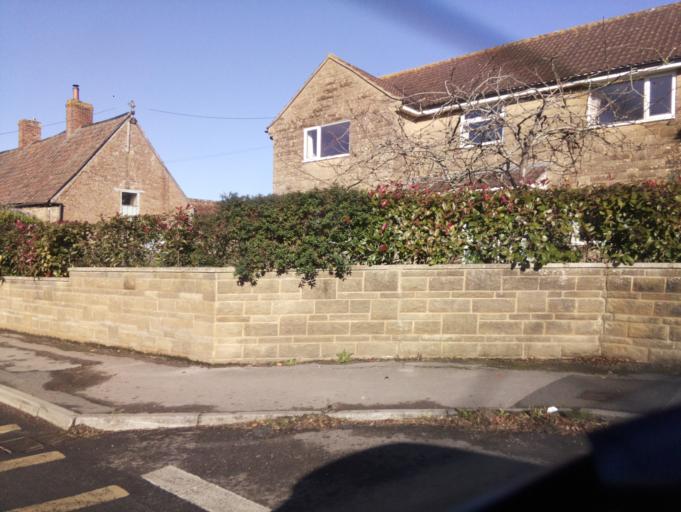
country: GB
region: England
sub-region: Somerset
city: Martock
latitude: 50.9832
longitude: -2.7508
